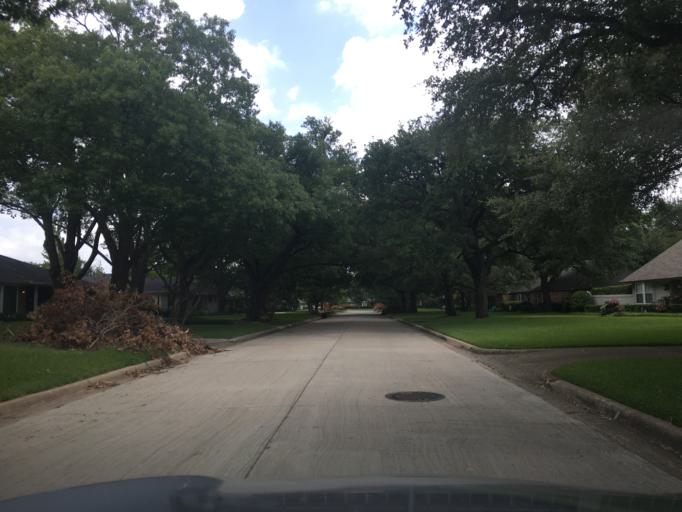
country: US
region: Texas
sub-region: Dallas County
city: Addison
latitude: 32.9089
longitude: -96.8329
